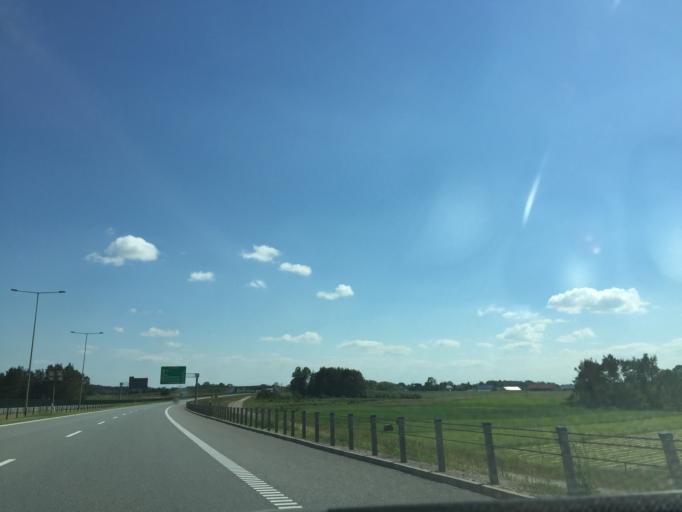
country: PL
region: Podlasie
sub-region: Suwalki
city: Suwalki
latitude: 54.0468
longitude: 22.8928
